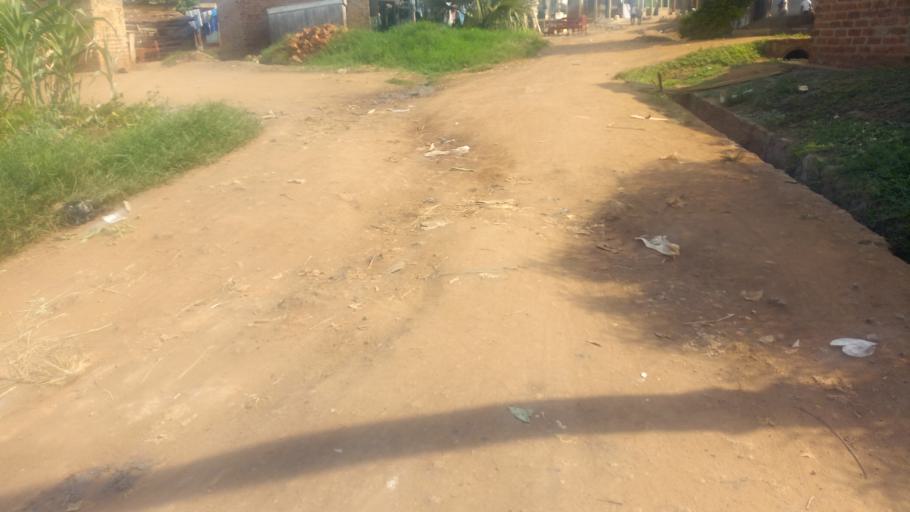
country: UG
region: Western Region
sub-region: Kiryandongo District
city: Kiryandongo
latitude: 1.8095
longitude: 32.0104
